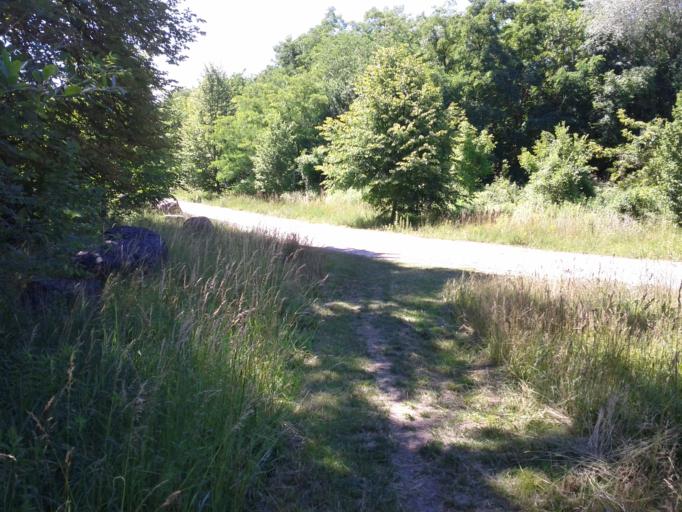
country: DE
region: Brandenburg
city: Woltersdorf
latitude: 52.4758
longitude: 13.7953
